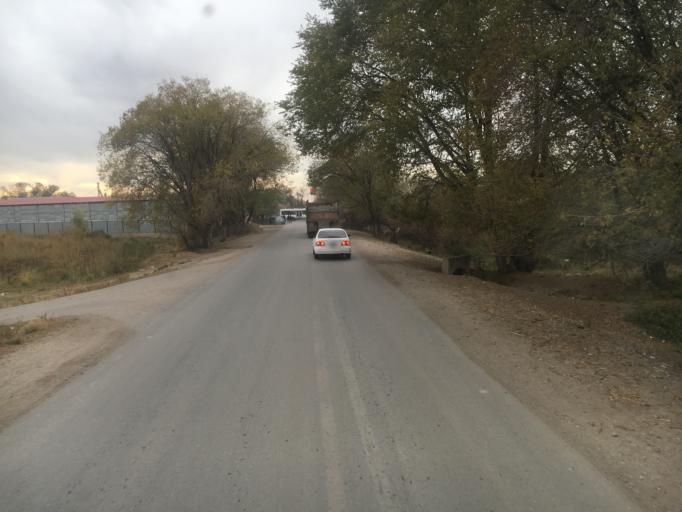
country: KZ
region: Almaty Oblysy
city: Energeticheskiy
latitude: 43.5860
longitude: 77.0632
